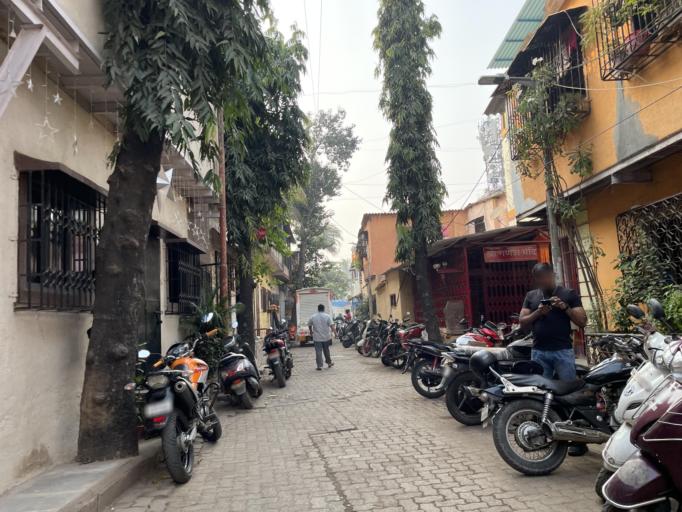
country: IN
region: Maharashtra
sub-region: Mumbai Suburban
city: Borivli
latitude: 19.1949
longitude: 72.8217
